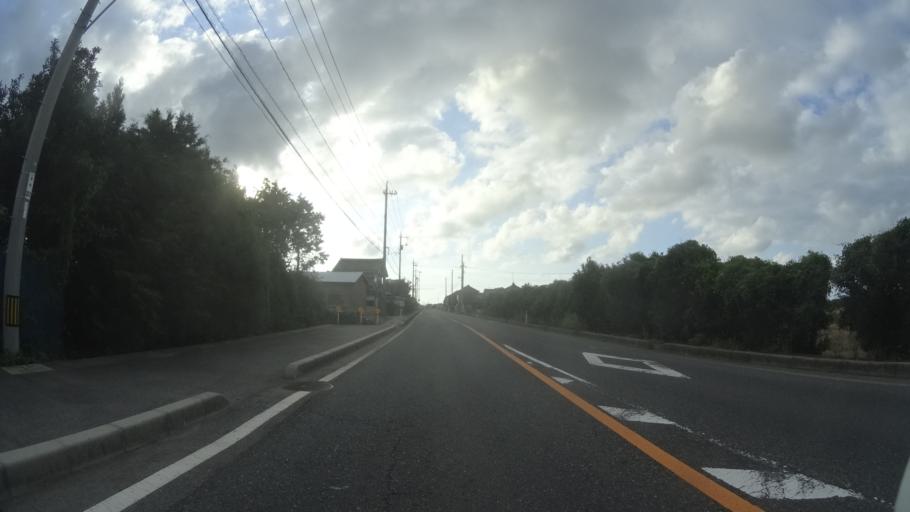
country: JP
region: Tottori
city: Kurayoshi
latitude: 35.5219
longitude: 133.5982
